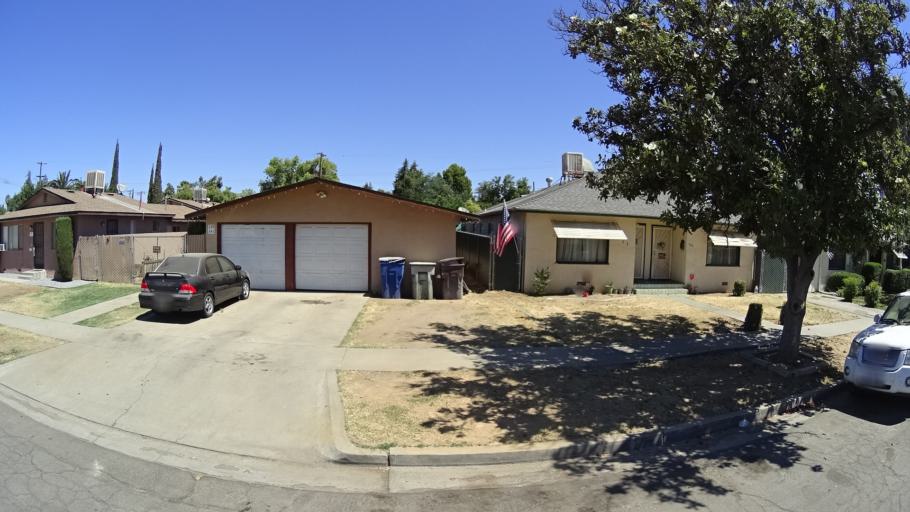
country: US
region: California
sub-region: Fresno County
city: Fresno
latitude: 36.7849
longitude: -119.8076
